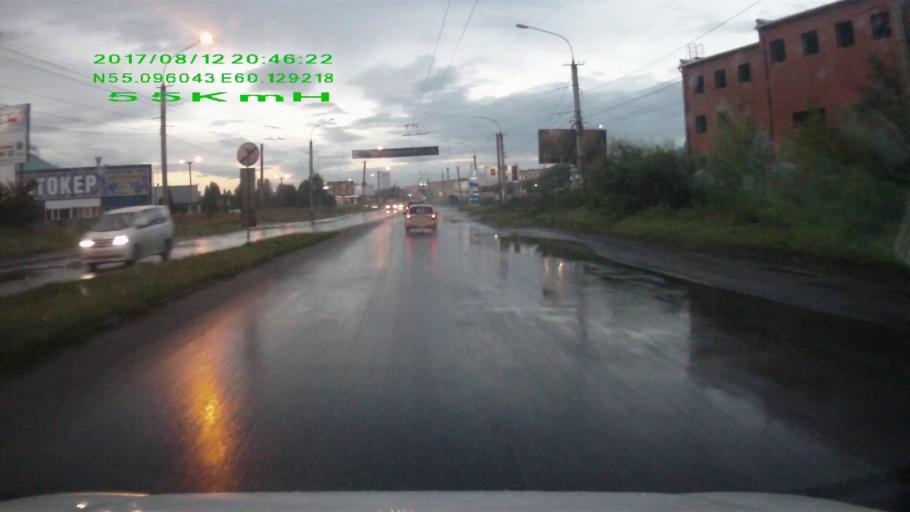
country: RU
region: Chelyabinsk
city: Turgoyak
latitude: 55.0961
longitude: 60.1292
